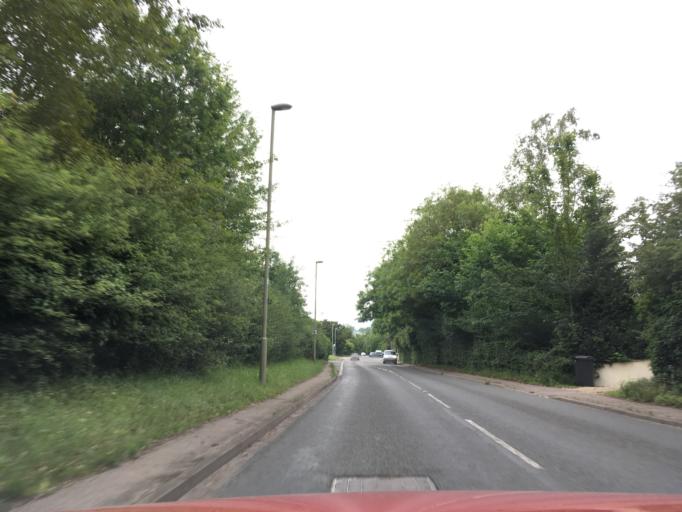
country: GB
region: England
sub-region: Oxfordshire
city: Boars Hill
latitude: 51.7006
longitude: -1.3040
